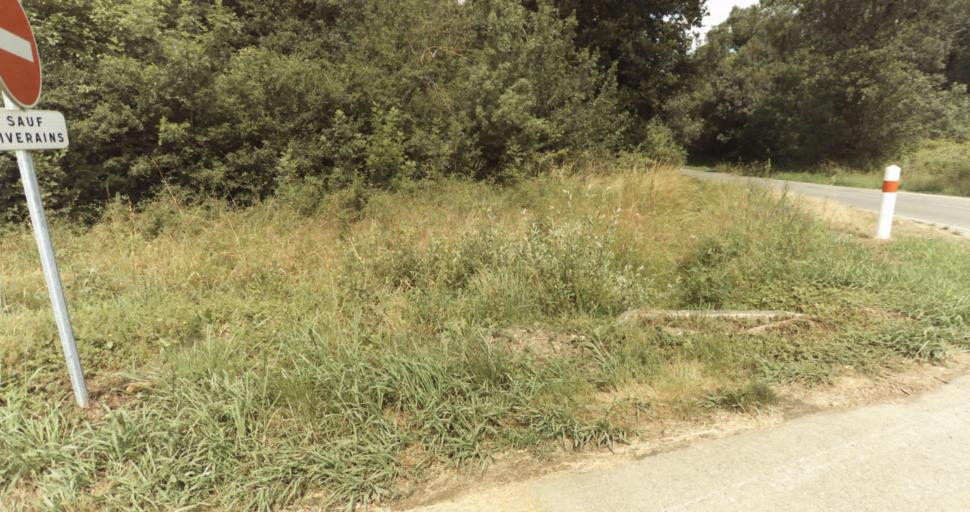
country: FR
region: Midi-Pyrenees
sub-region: Departement de la Haute-Garonne
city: Fontenilles
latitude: 43.5675
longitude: 1.1942
